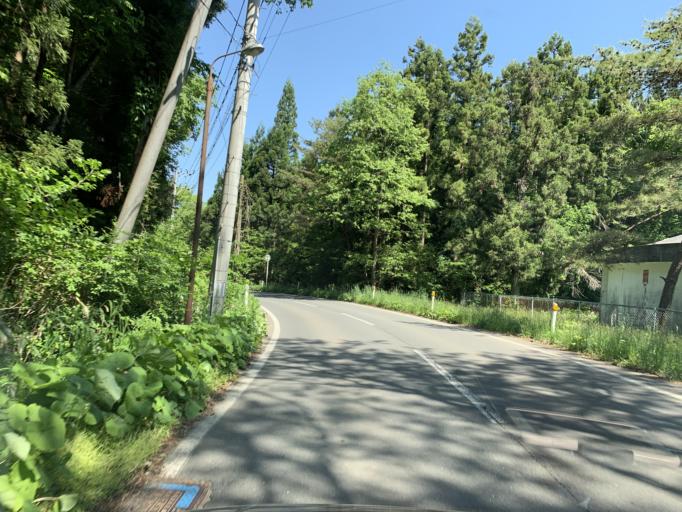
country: JP
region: Iwate
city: Mizusawa
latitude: 39.1631
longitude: 141.0664
